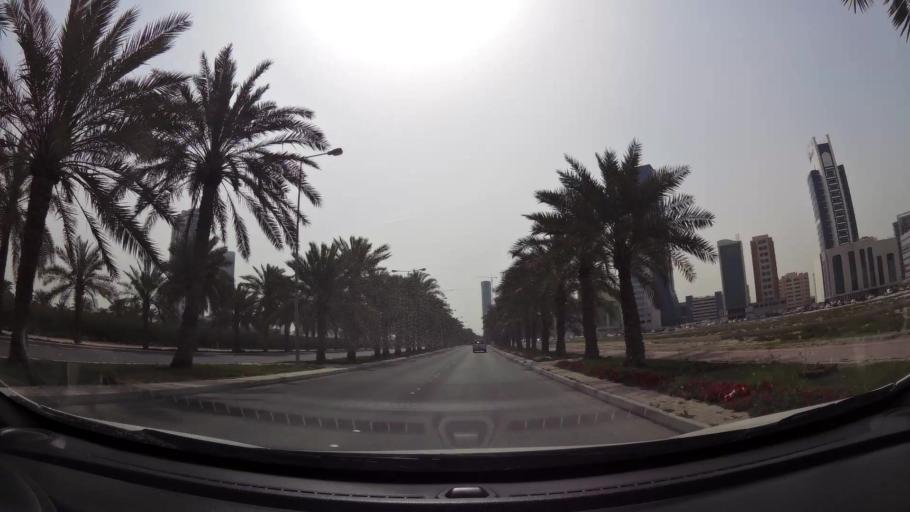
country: BH
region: Manama
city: Jidd Hafs
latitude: 26.2401
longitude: 50.5408
